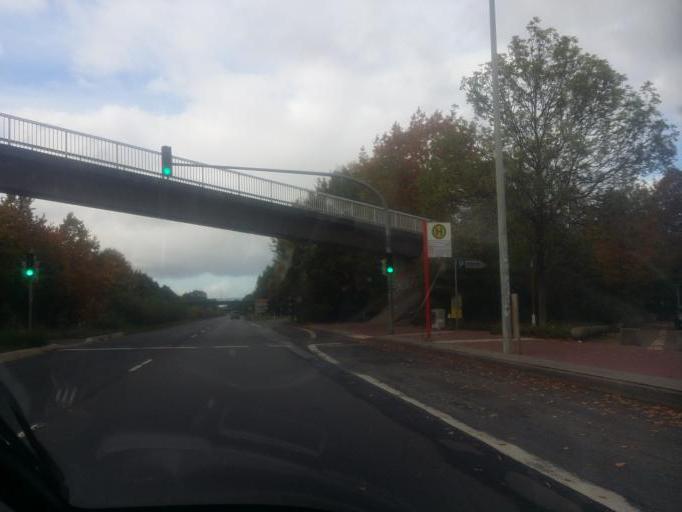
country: DE
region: Schleswig-Holstein
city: Halstenbek
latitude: 53.6012
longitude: 9.8364
